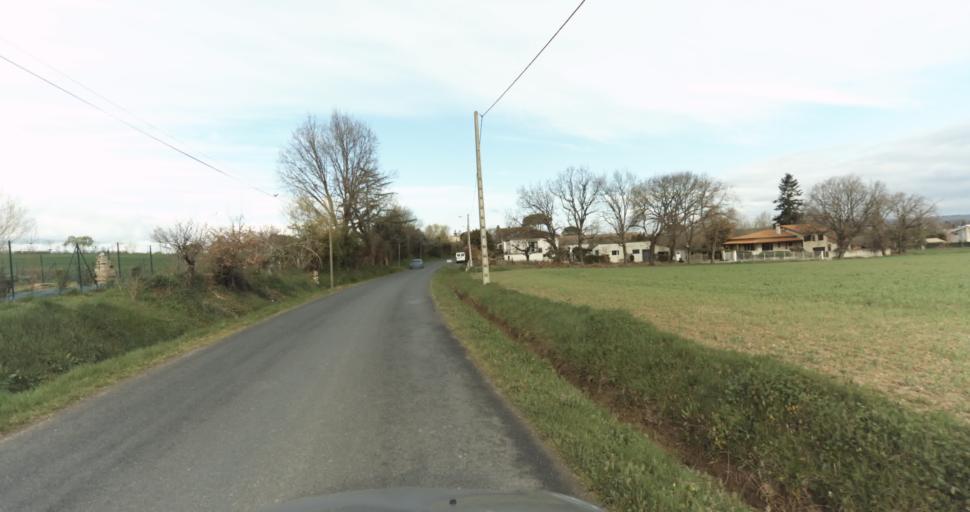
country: FR
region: Midi-Pyrenees
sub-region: Departement du Tarn
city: Puygouzon
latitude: 43.9103
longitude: 2.1759
